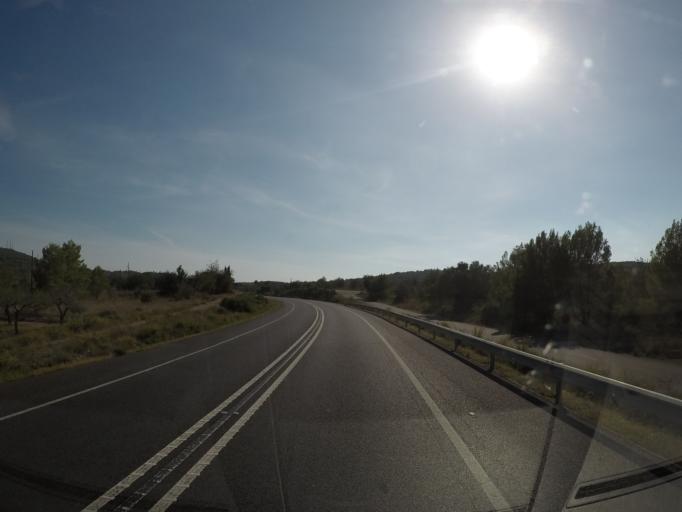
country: ES
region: Catalonia
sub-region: Provincia de Tarragona
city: El Perello
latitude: 40.8877
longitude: 0.7198
